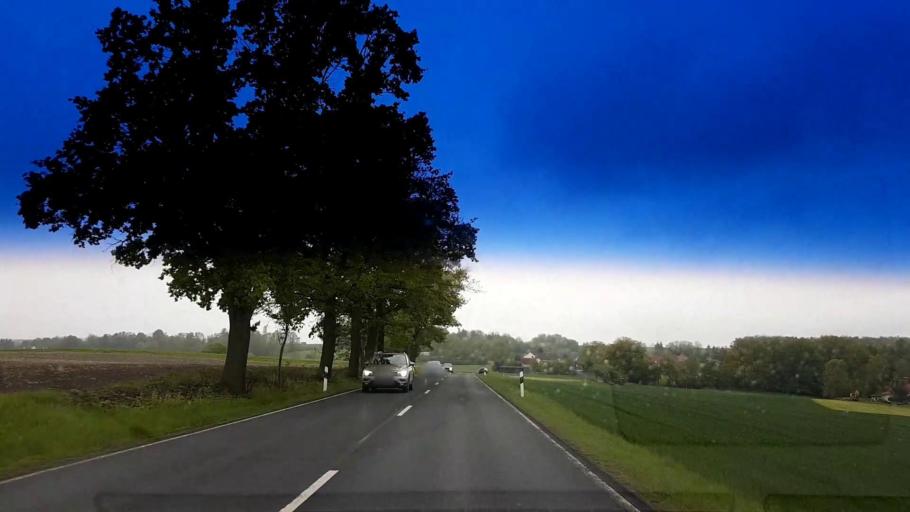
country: DE
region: Bavaria
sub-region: Upper Franconia
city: Gesees
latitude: 50.0146
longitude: 11.6331
